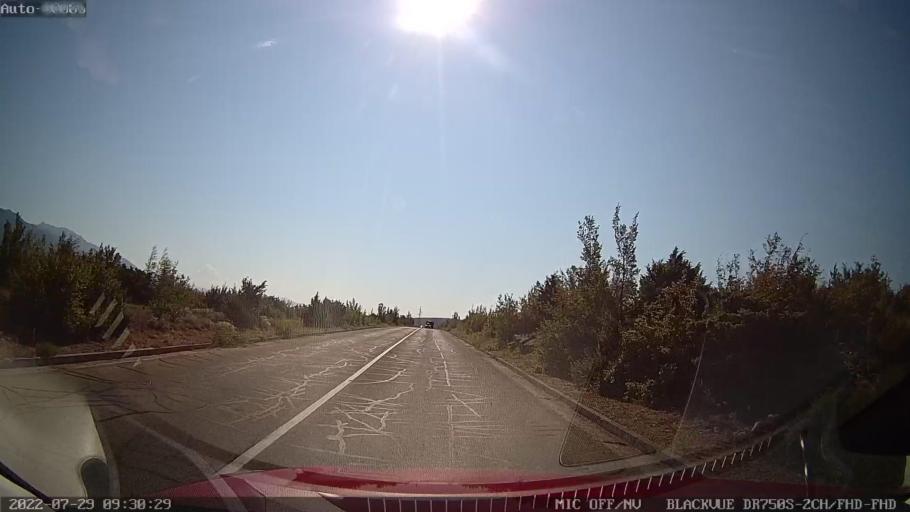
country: HR
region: Zadarska
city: Obrovac
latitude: 44.1936
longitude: 15.6867
